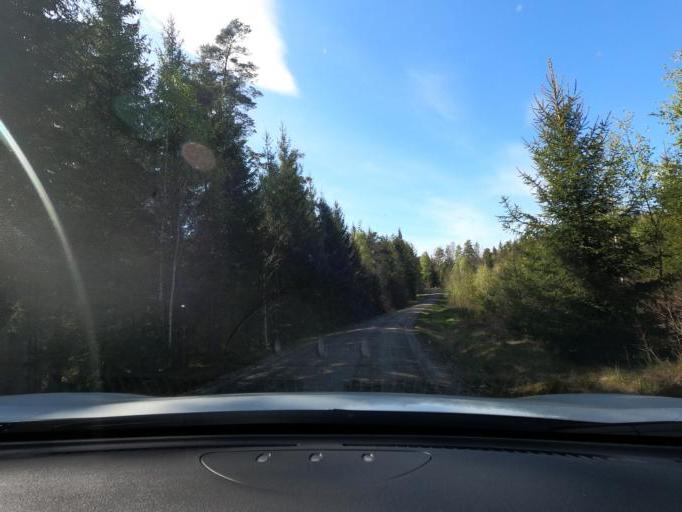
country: SE
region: Vaestra Goetaland
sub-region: Harryda Kommun
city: Ravlanda
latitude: 57.5930
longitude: 12.4826
